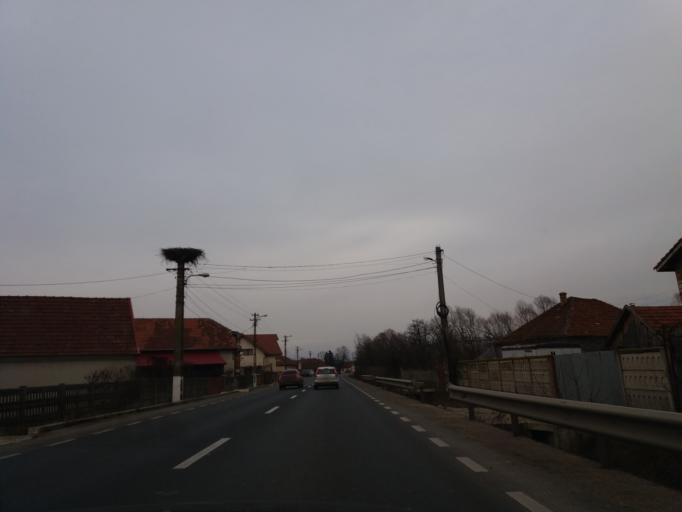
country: RO
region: Hunedoara
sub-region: Comuna Bacia
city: Bacia
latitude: 45.7720
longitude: 23.0017
